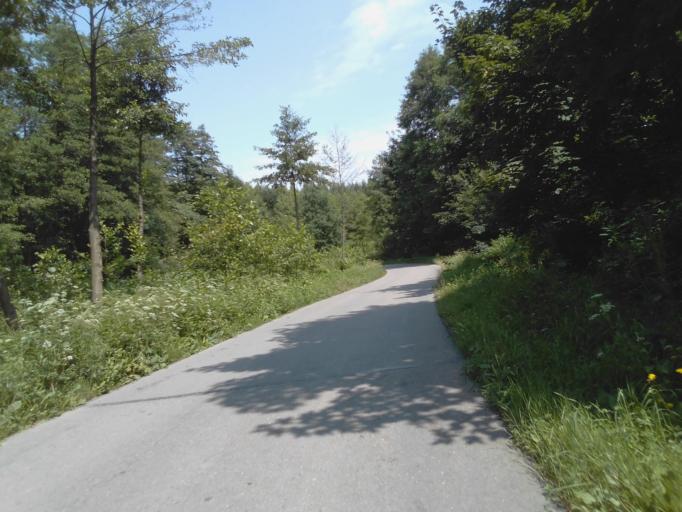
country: PL
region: Subcarpathian Voivodeship
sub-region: Powiat strzyzowski
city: Frysztak
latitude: 49.7871
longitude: 21.6058
